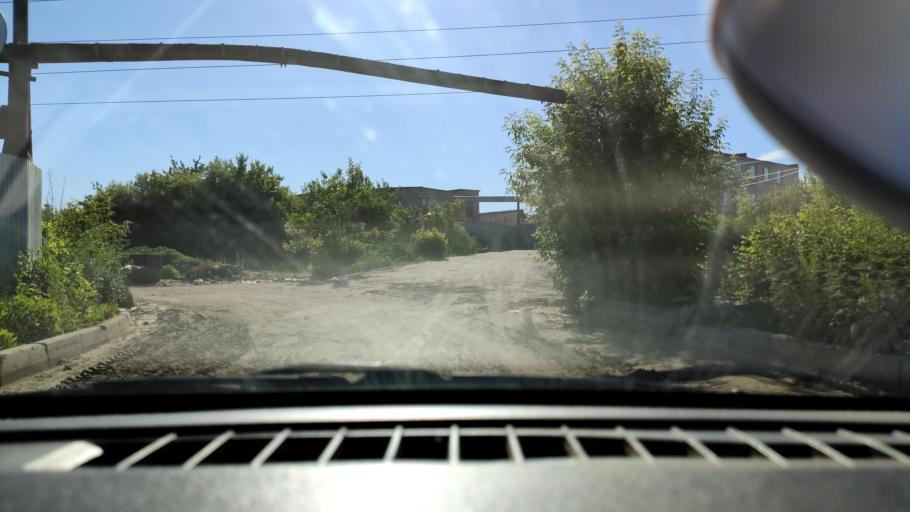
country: RU
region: Samara
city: Rozhdestveno
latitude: 53.1675
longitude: 50.0700
